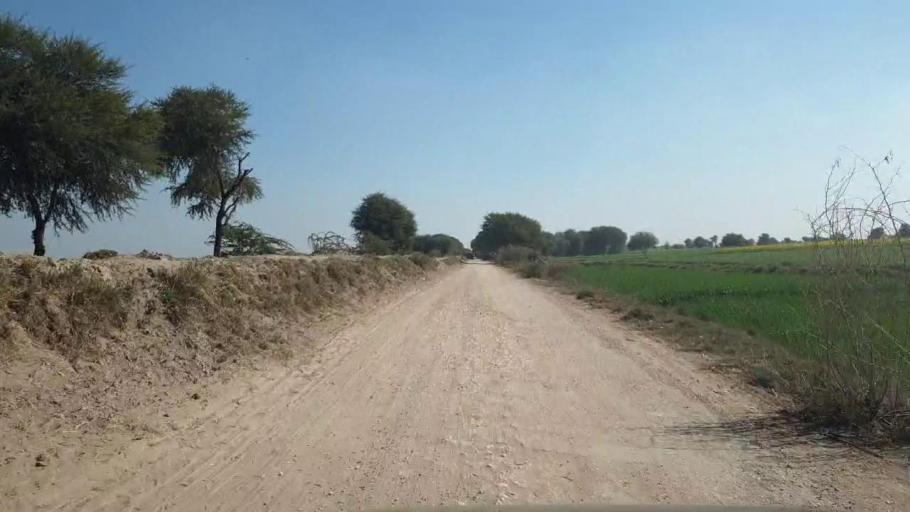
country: PK
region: Sindh
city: Shahpur Chakar
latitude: 26.1427
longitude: 68.6528
